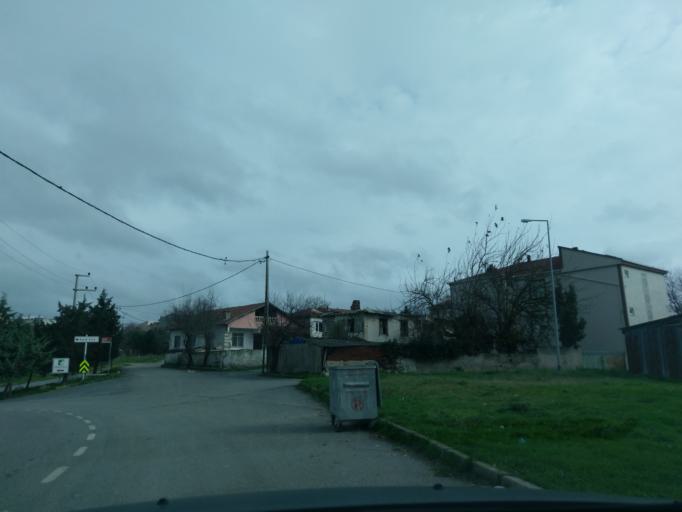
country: TR
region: Istanbul
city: Ortakoy
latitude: 41.1027
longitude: 28.3736
